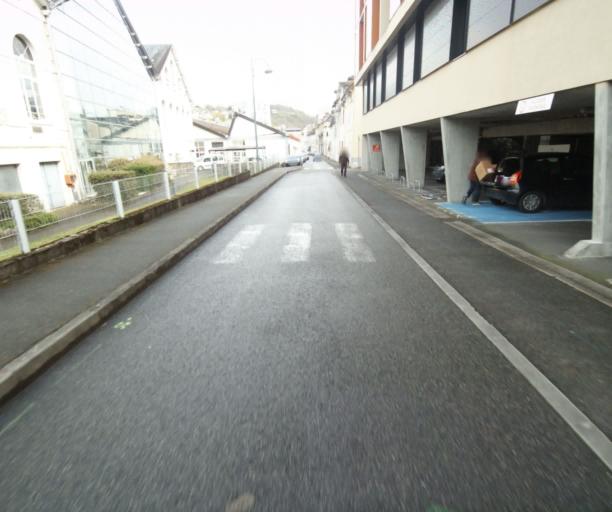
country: FR
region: Limousin
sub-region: Departement de la Correze
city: Tulle
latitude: 45.2605
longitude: 1.7499
